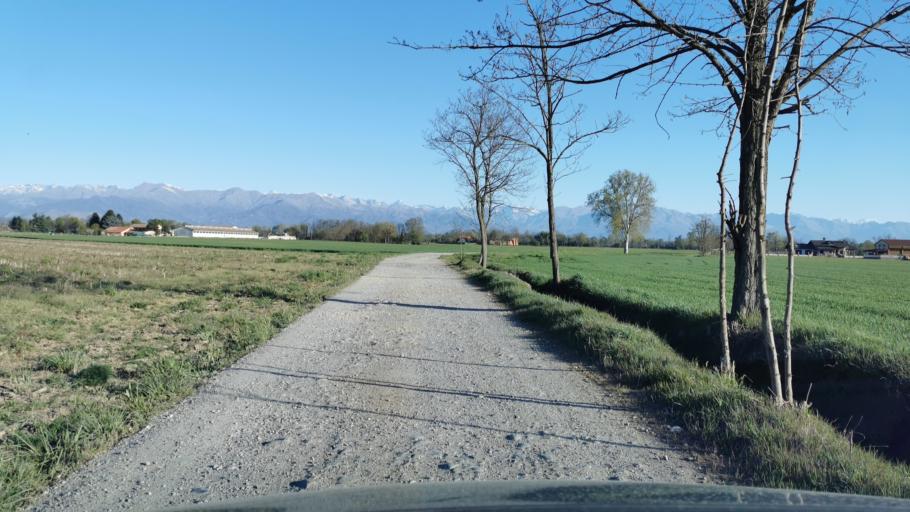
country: IT
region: Piedmont
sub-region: Provincia di Torino
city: Leini
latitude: 45.1954
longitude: 7.6844
